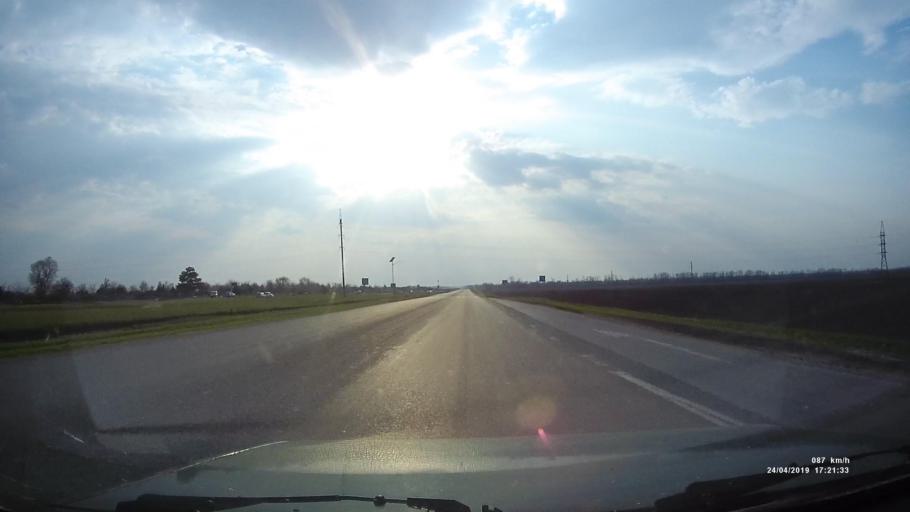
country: RU
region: Rostov
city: Gigant
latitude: 46.5193
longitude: 41.3295
